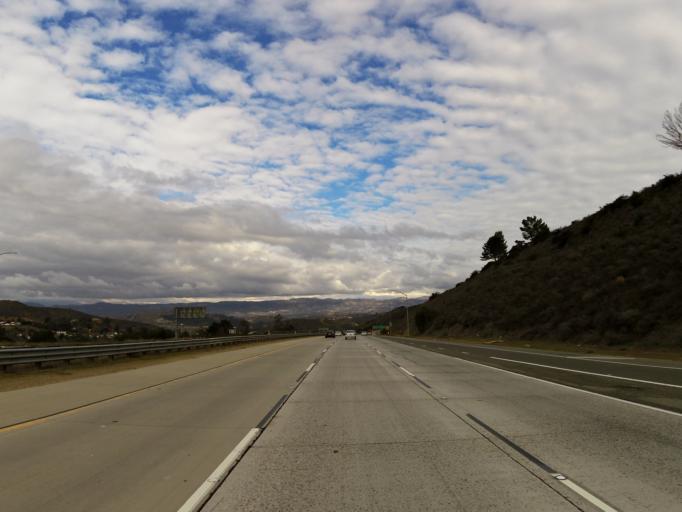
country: US
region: California
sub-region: Ventura County
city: Thousand Oaks
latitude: 34.2305
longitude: -118.8454
